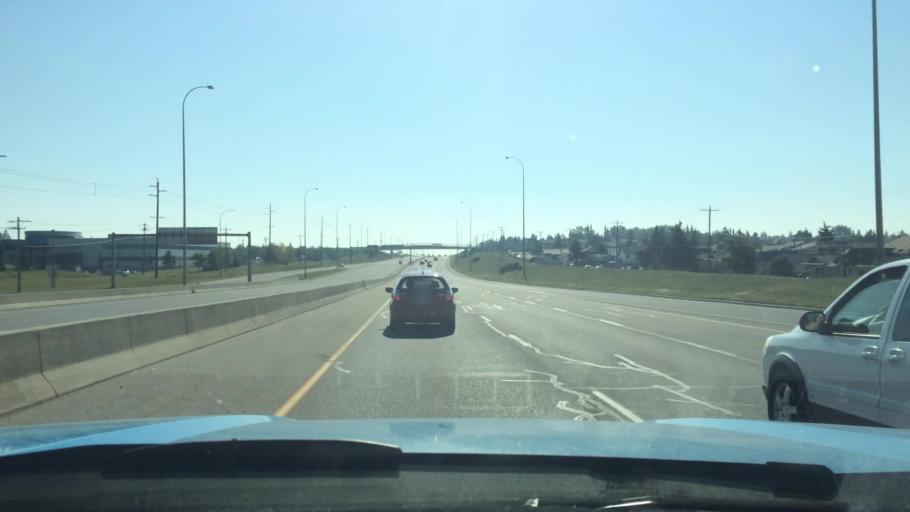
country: CA
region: Alberta
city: Calgary
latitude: 51.0959
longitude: -113.9790
